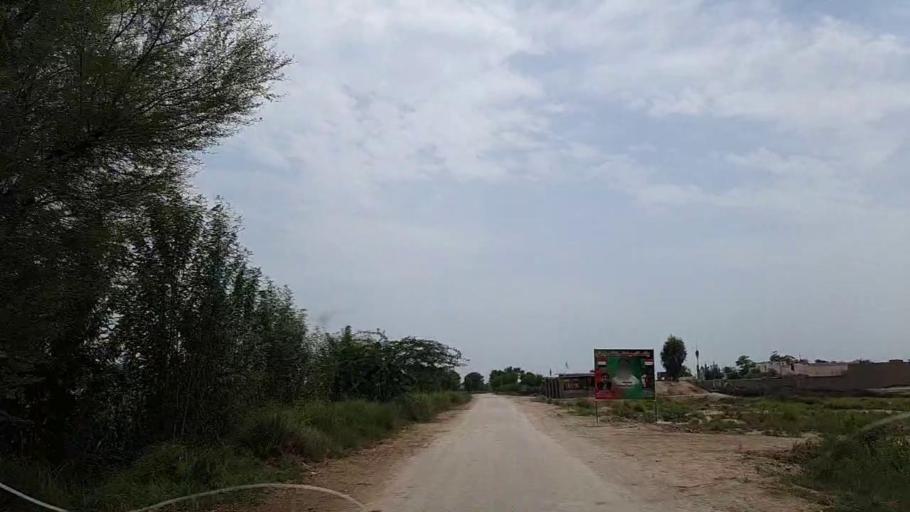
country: PK
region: Sindh
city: Tharu Shah
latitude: 26.9290
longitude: 68.1044
